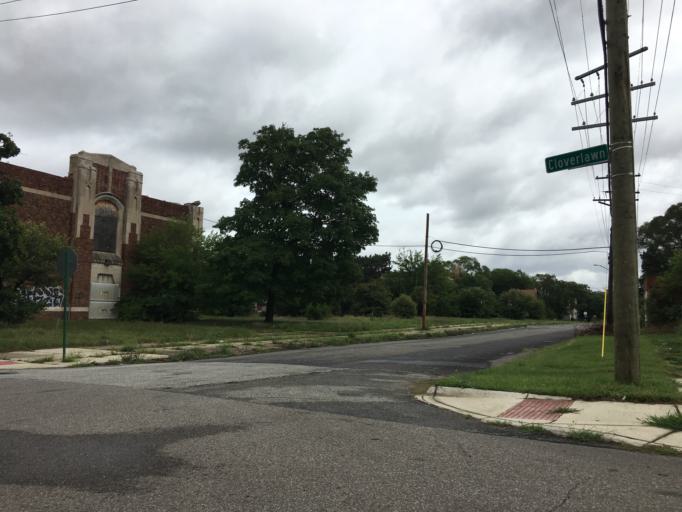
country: US
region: Michigan
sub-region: Wayne County
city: Highland Park
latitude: 42.4062
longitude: -83.1526
